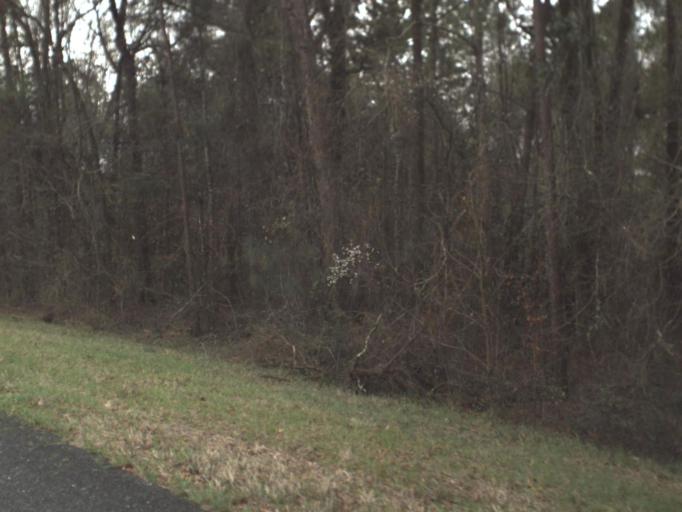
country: US
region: Florida
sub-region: Leon County
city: Woodville
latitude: 30.4101
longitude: -84.0686
